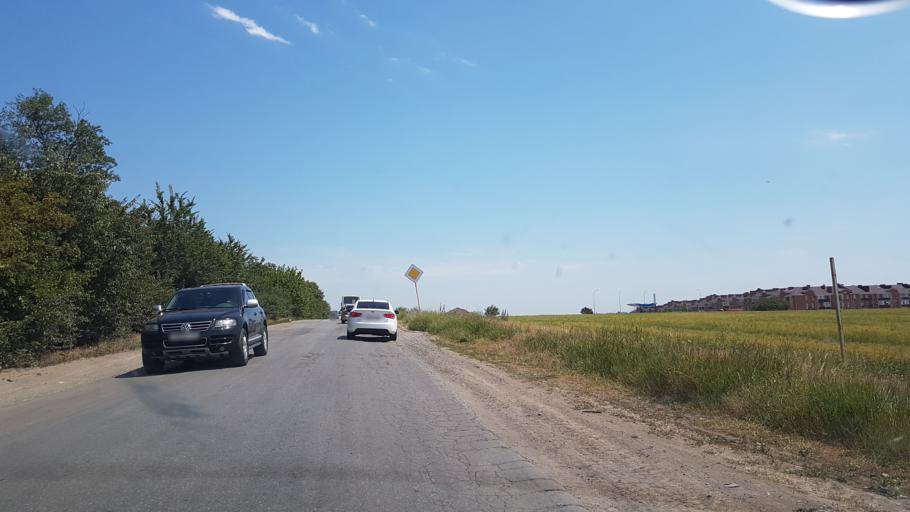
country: RU
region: Rostov
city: Temernik
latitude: 47.3231
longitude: 39.7425
